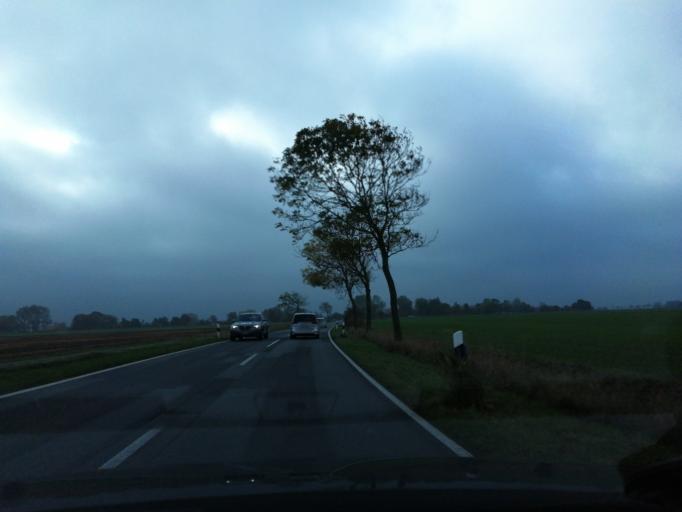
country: DE
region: Lower Saxony
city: Wangerooge
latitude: 53.6896
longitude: 7.8559
